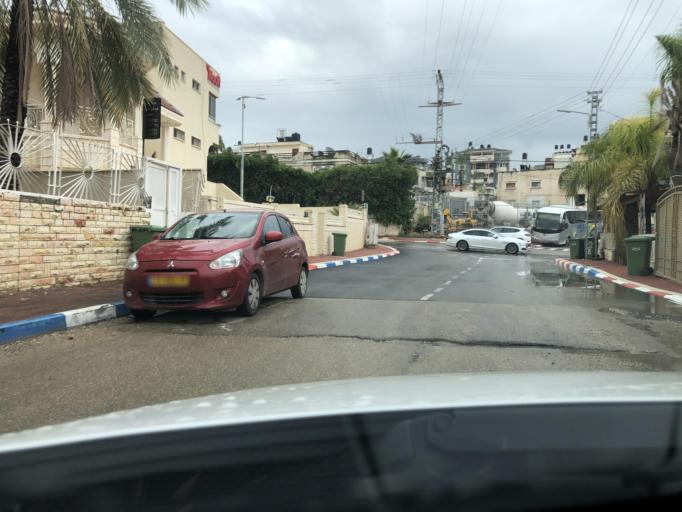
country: IL
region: Central District
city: Kafr Qasim
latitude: 32.1119
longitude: 34.9753
